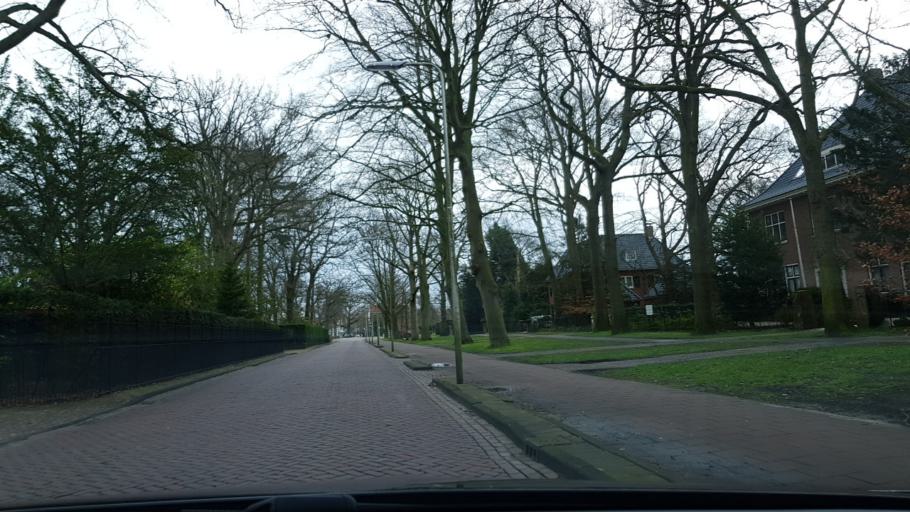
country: NL
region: North Holland
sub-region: Gemeente Heemstede
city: Heemstede
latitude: 52.3467
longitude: 4.6158
